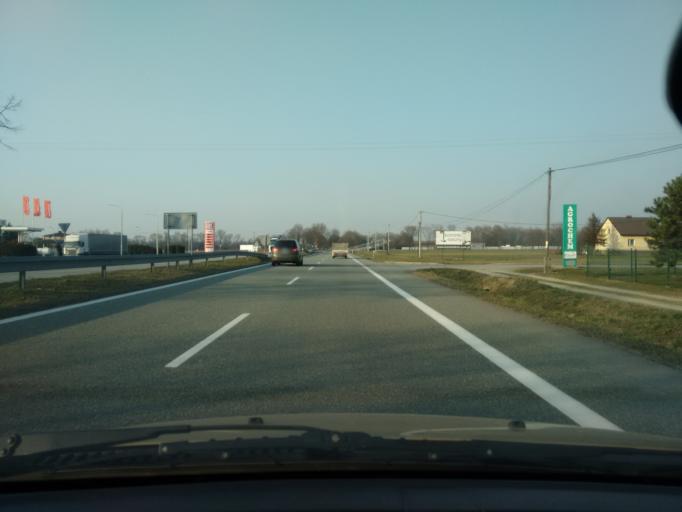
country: PL
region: Silesian Voivodeship
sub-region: Powiat cieszynski
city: Drogomysl
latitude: 49.8796
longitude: 18.7445
